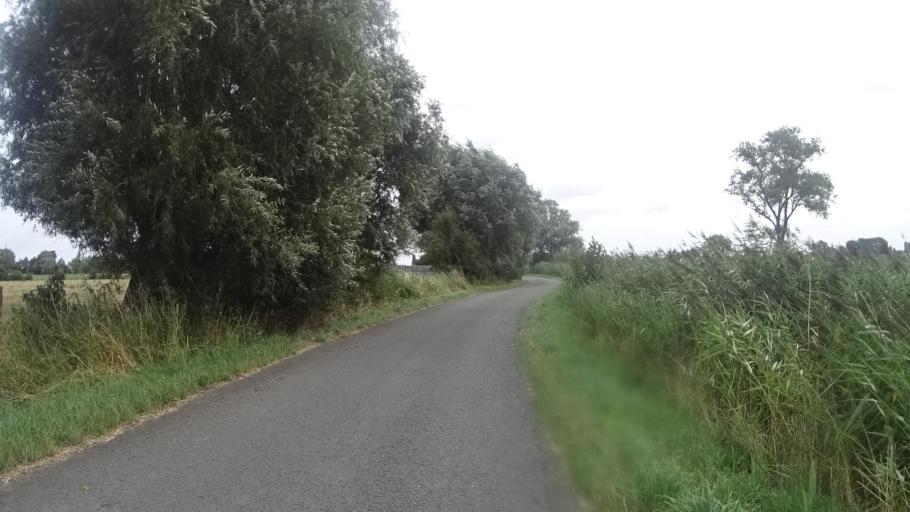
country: BE
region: Flanders
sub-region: Provincie West-Vlaanderen
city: Diksmuide
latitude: 51.0470
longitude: 2.8897
